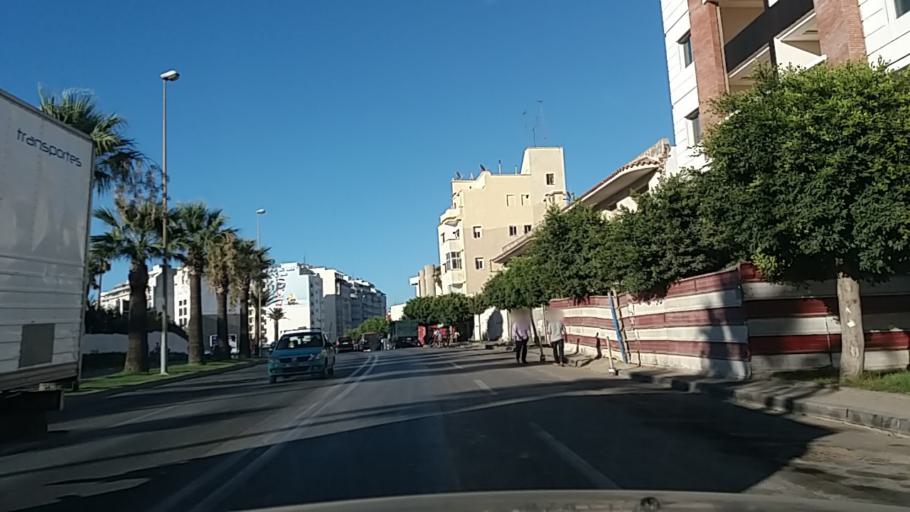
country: MA
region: Tanger-Tetouan
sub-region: Tanger-Assilah
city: Tangier
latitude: 35.7661
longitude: -5.8161
